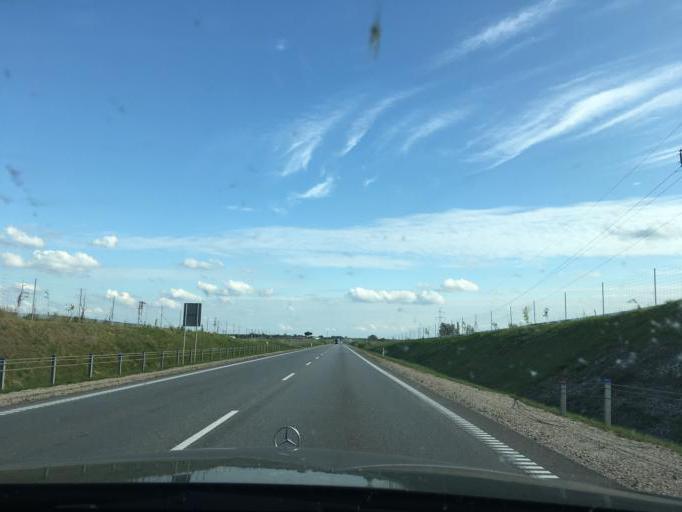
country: PL
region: Podlasie
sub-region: Powiat augustowski
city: Augustow
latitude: 53.8628
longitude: 22.9016
